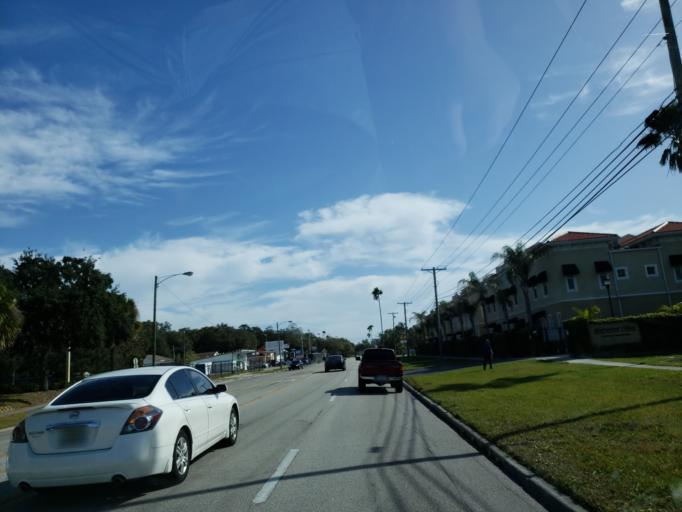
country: US
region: Florida
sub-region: Hillsborough County
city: Tampa
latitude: 27.8936
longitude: -82.5015
